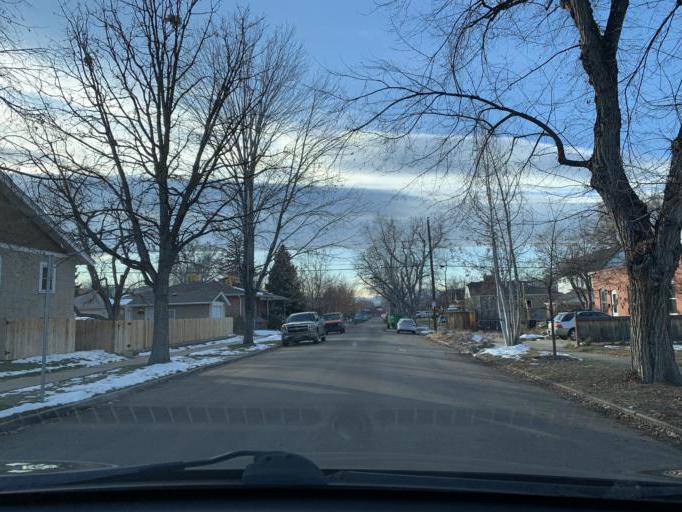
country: US
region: Colorado
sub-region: Jefferson County
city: Edgewater
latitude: 39.7725
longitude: -105.0405
